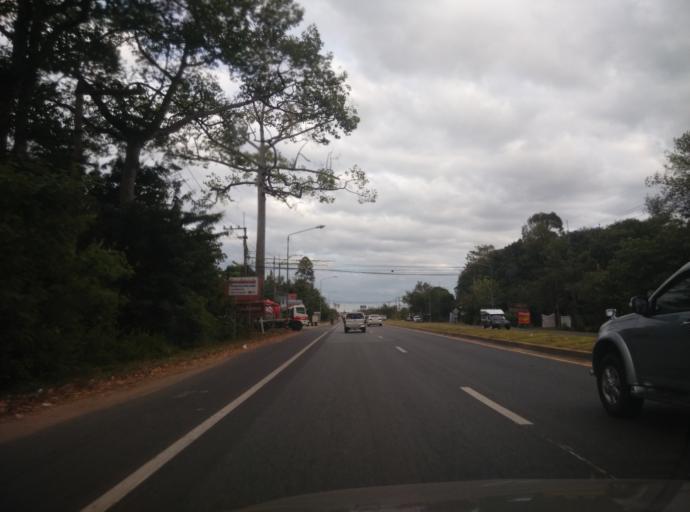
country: TH
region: Sisaket
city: Si Sa Ket
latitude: 15.1254
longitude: 104.2904
